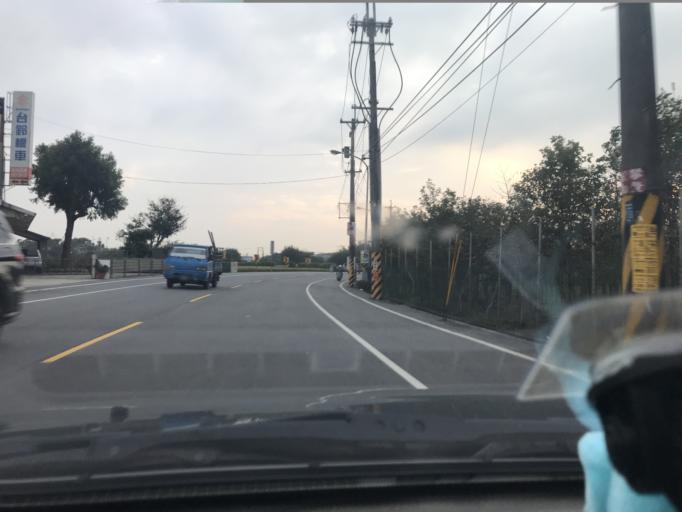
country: TW
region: Taiwan
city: Daxi
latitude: 24.8960
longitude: 121.2263
